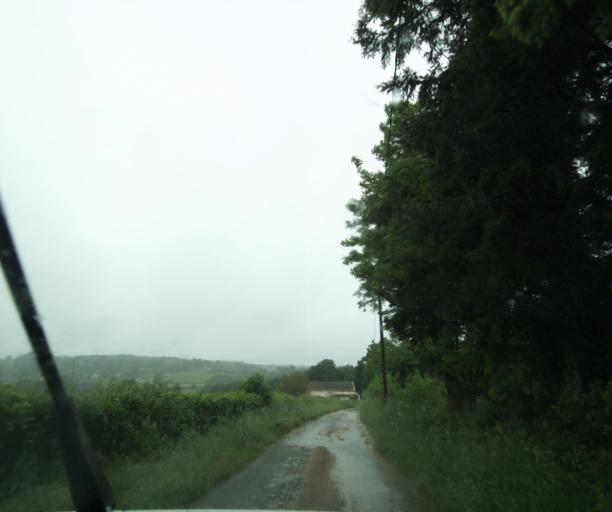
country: FR
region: Bourgogne
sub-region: Departement de Saone-et-Loire
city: Charolles
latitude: 46.3886
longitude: 4.3303
